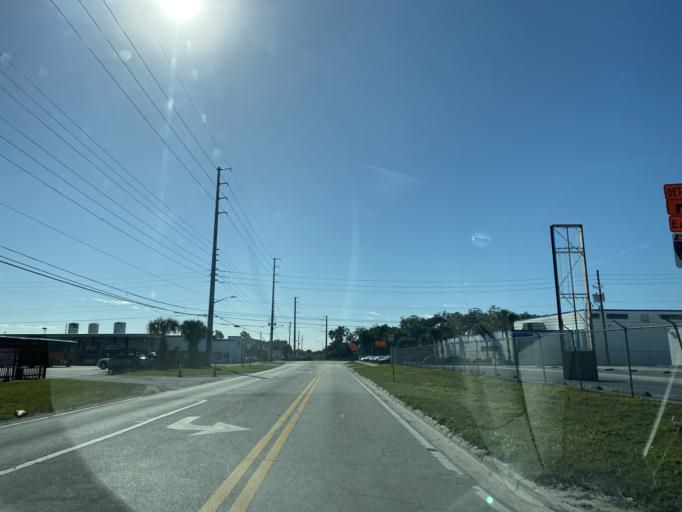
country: US
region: Florida
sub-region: Orange County
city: Holden Heights
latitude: 28.5165
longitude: -81.3848
